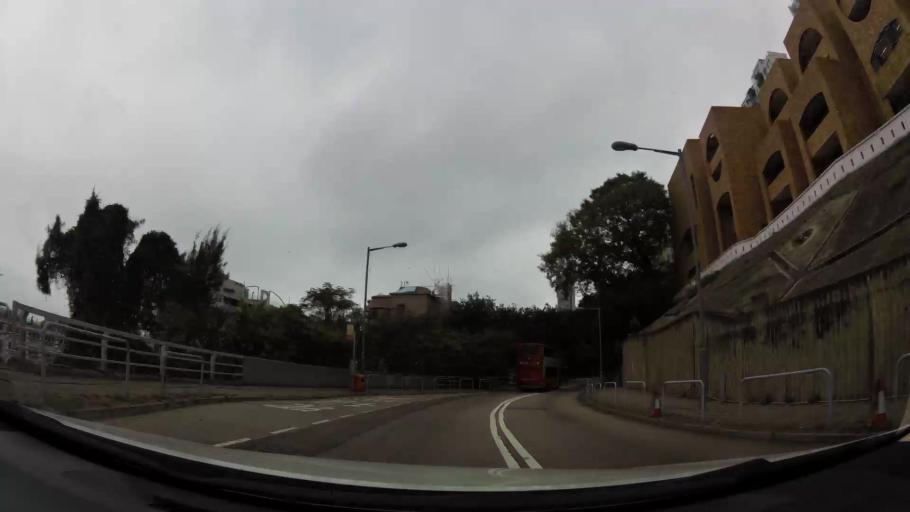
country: HK
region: Central and Western
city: Central
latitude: 22.2722
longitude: 114.1208
